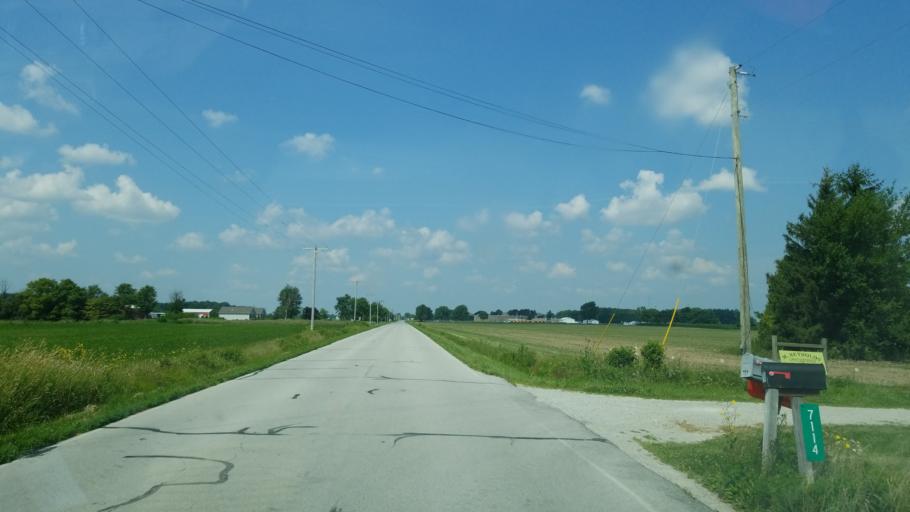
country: US
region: Ohio
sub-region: Seneca County
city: Fostoria
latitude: 41.2534
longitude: -83.5380
